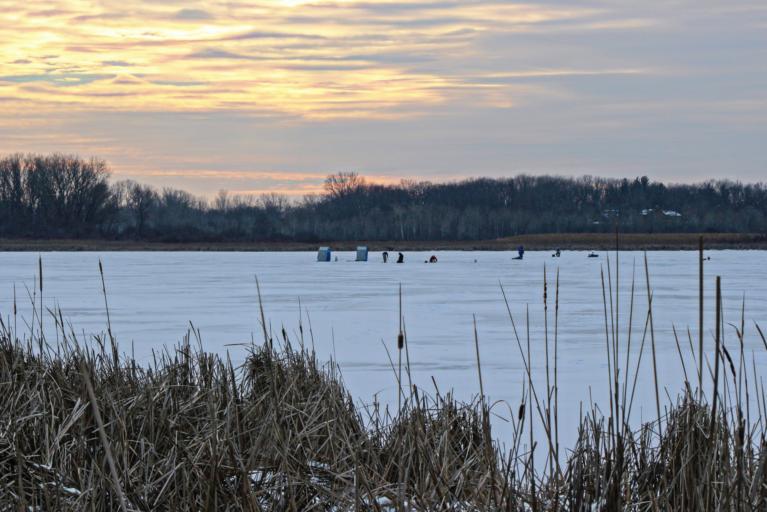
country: US
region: Wisconsin
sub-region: Jefferson County
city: Lake Mills
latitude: 43.0461
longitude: -88.9176
